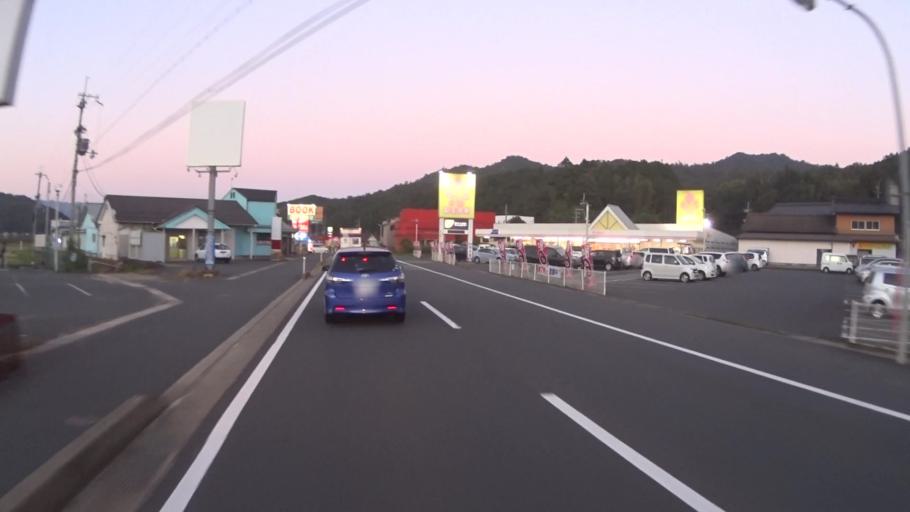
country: JP
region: Kyoto
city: Miyazu
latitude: 35.5383
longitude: 135.1282
